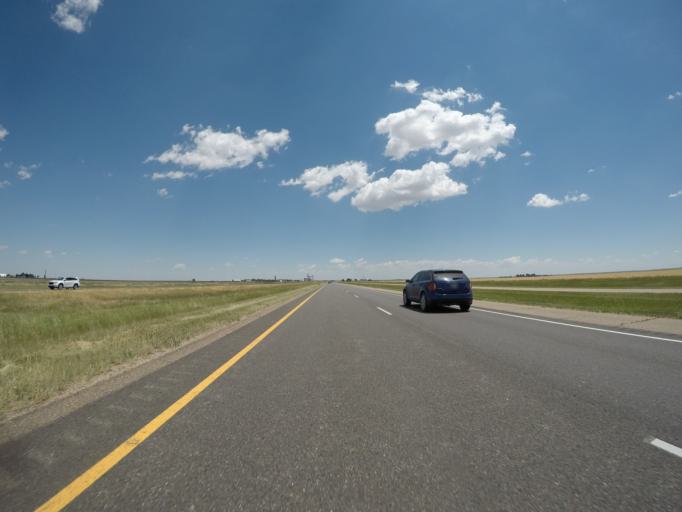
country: US
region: Colorado
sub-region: Lincoln County
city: Hugo
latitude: 39.2823
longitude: -103.3009
